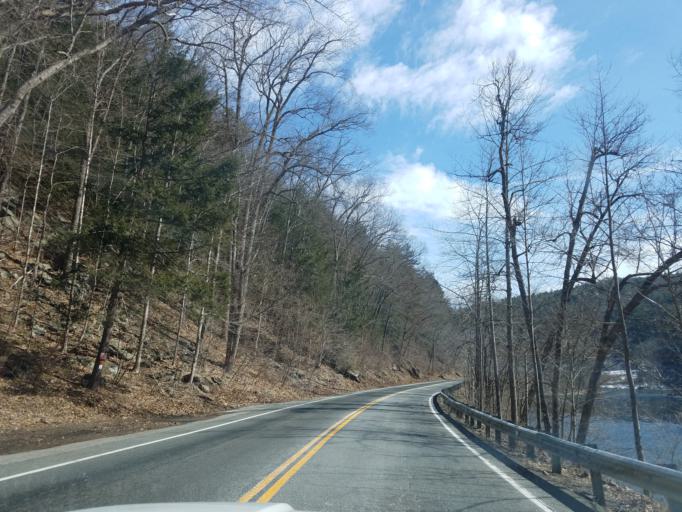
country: US
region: Connecticut
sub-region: Litchfield County
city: Canaan
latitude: 41.8689
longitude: -73.3680
